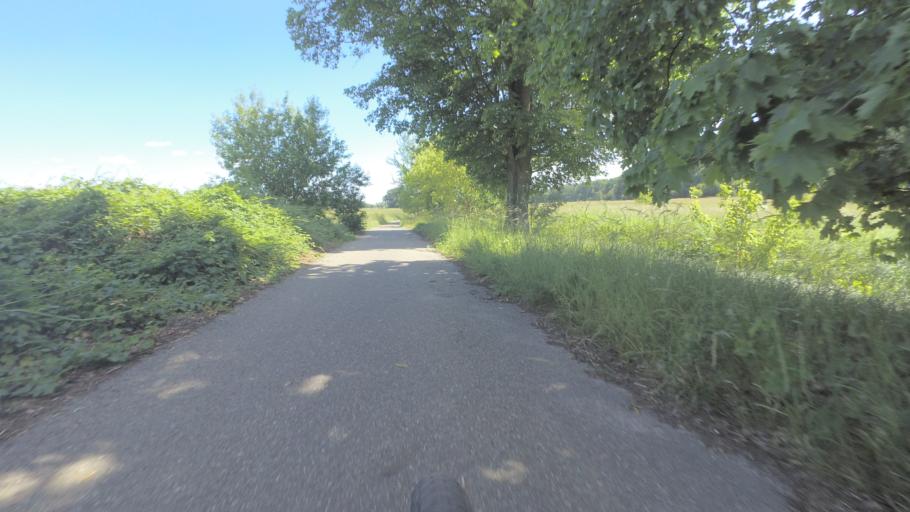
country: DE
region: Brandenburg
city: Rangsdorf
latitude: 52.3053
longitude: 13.4424
